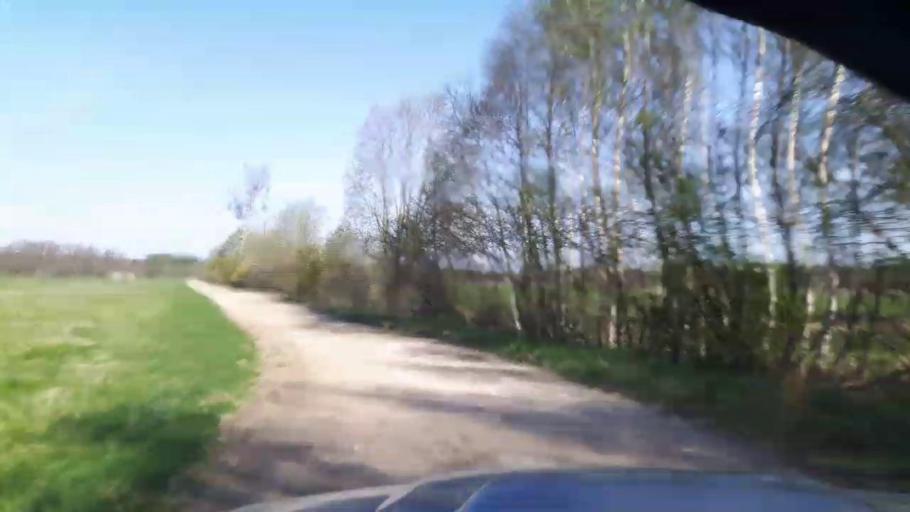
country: EE
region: Paernumaa
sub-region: Tootsi vald
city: Tootsi
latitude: 58.4863
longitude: 24.9289
